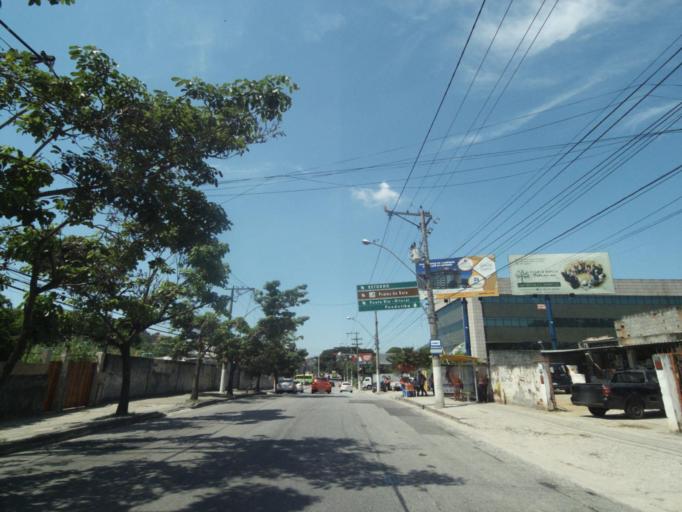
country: BR
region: Rio de Janeiro
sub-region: Niteroi
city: Niteroi
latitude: -22.9077
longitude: -43.0637
